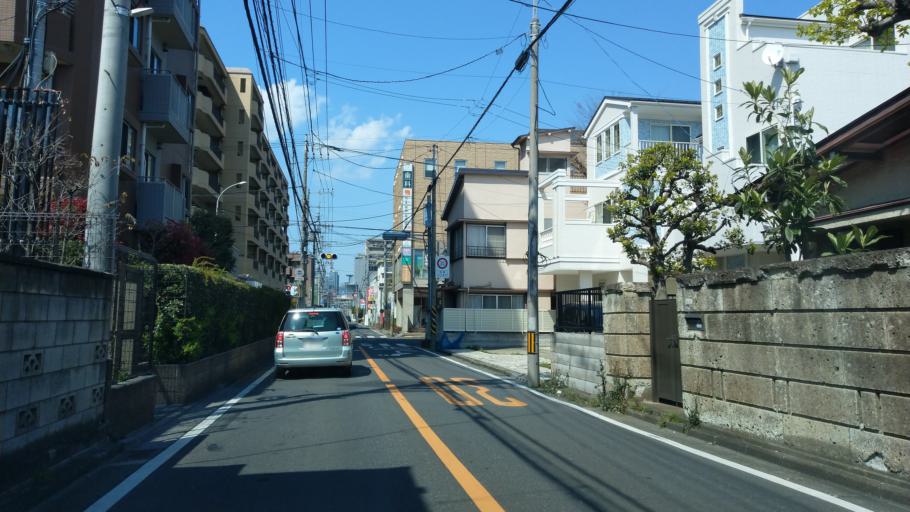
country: JP
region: Saitama
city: Yono
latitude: 35.8701
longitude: 139.6370
